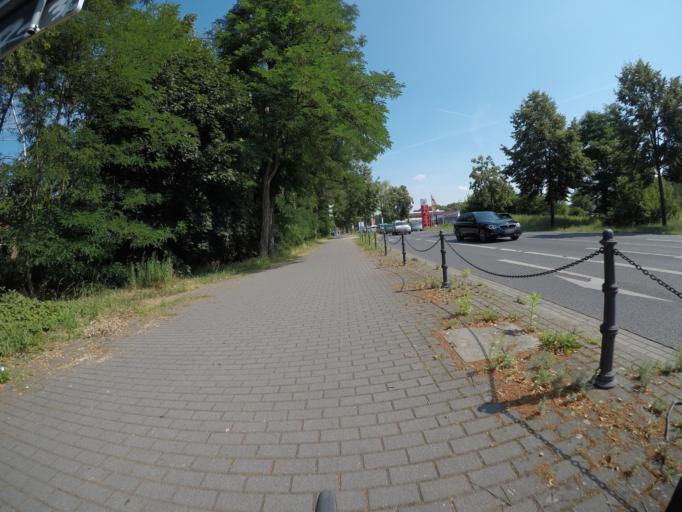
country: DE
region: Brandenburg
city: Bernau bei Berlin
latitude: 52.6696
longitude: 13.5827
